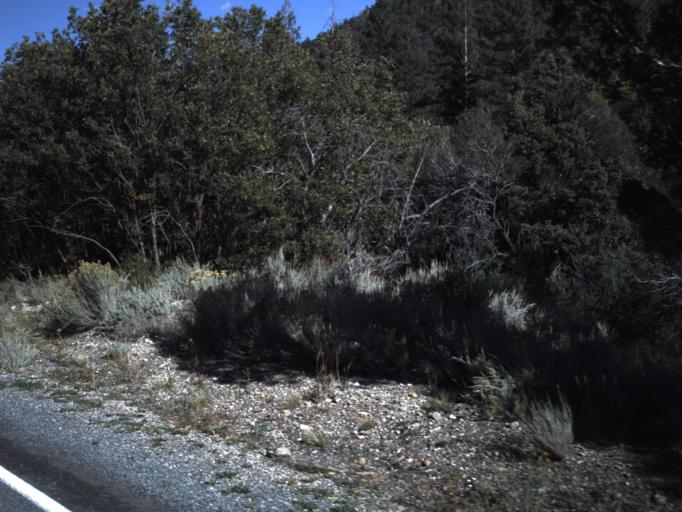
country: US
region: Utah
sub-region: Iron County
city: Parowan
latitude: 37.7691
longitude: -112.8443
